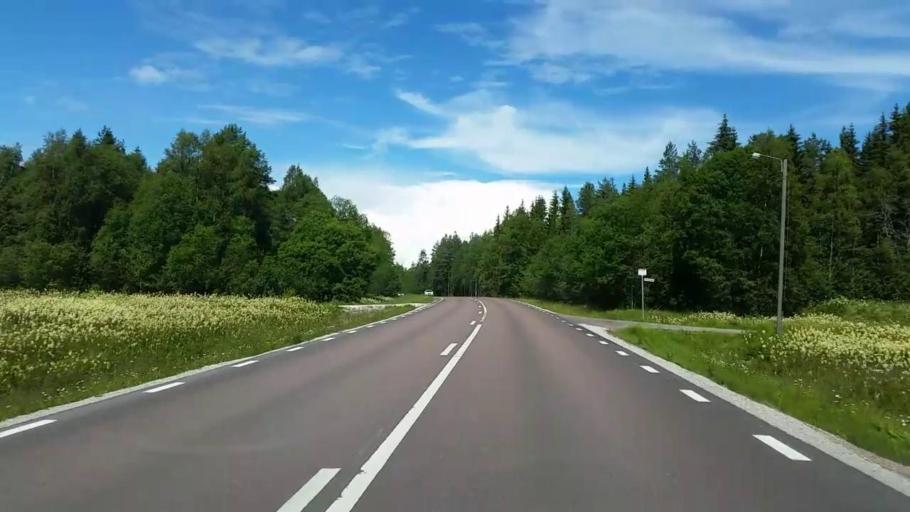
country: SE
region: Dalarna
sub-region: Rattviks Kommun
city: Raettvik
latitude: 61.0248
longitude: 15.2096
